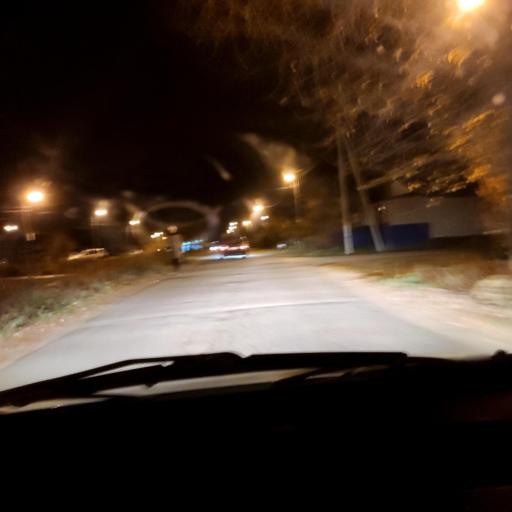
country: RU
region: Bashkortostan
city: Avdon
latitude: 54.7049
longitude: 55.8233
